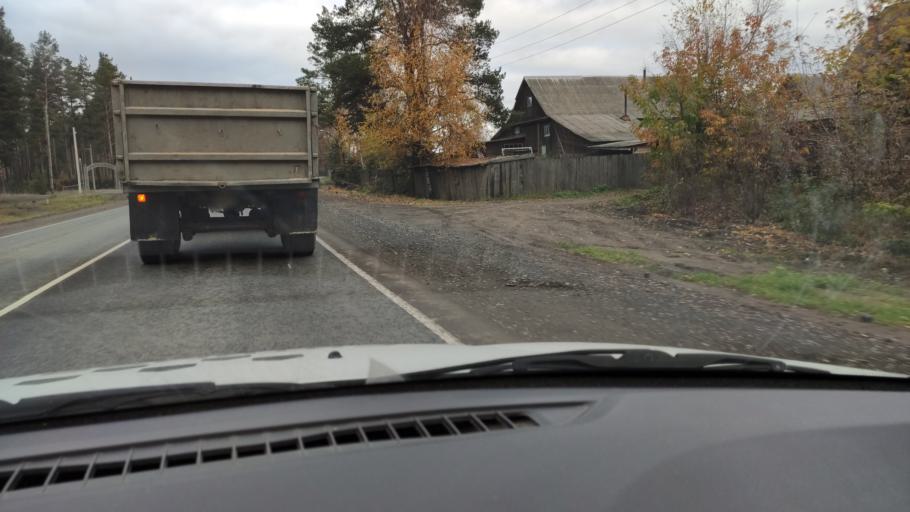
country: RU
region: Kirov
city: Belaya Kholunitsa
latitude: 58.8519
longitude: 50.8309
